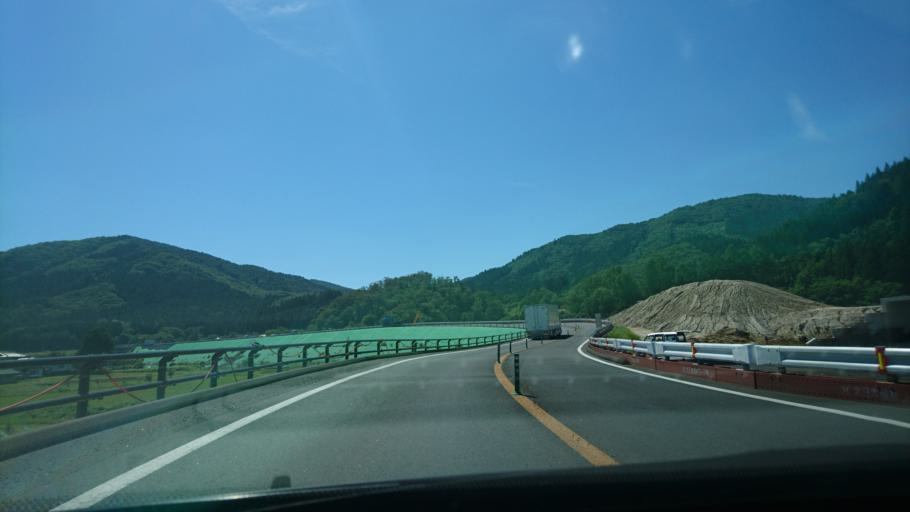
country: JP
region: Iwate
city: Tono
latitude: 39.2656
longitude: 141.5895
